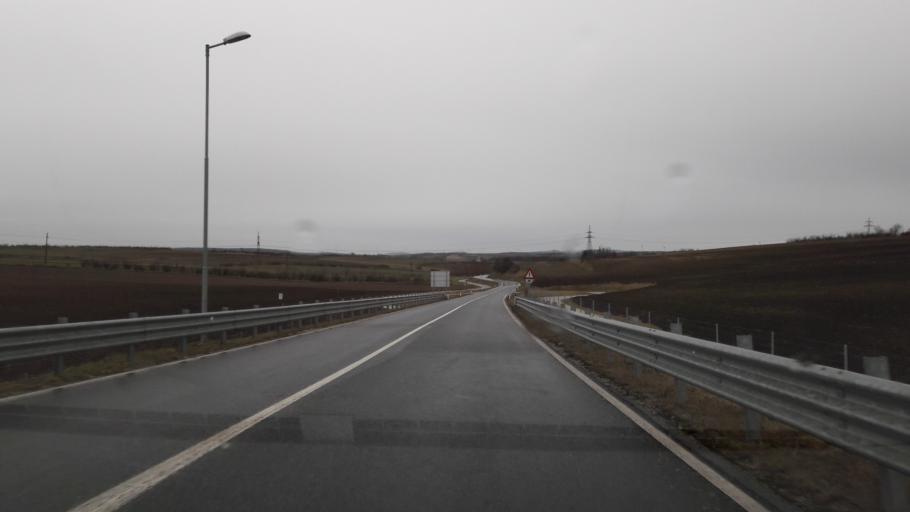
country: AT
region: Lower Austria
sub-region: Politischer Bezirk Mistelbach
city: Hochleithen
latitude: 48.4315
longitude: 16.5479
